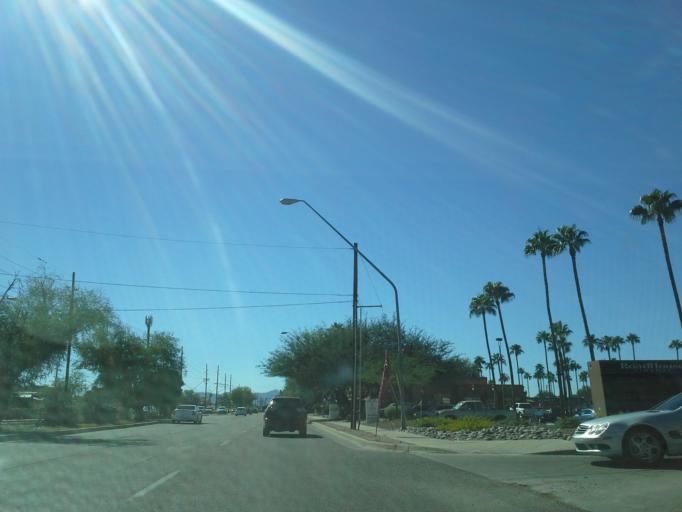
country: US
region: Arizona
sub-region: Pima County
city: Tucson
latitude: 32.2508
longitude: -110.8890
